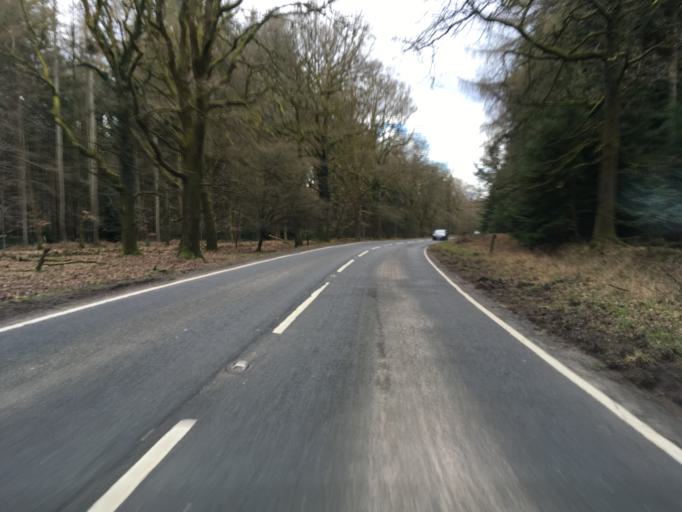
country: GB
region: England
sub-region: Gloucestershire
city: Cinderford
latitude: 51.8093
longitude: -2.5309
